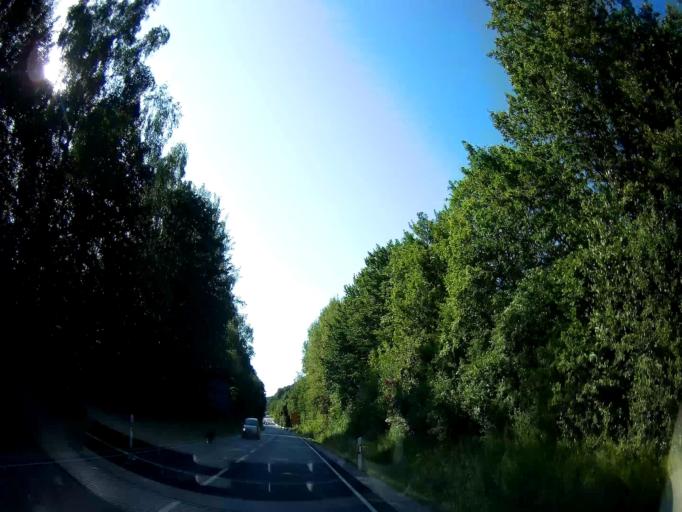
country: DE
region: Bavaria
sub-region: Upper Bavaria
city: Stammham
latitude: 48.2569
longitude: 12.9041
